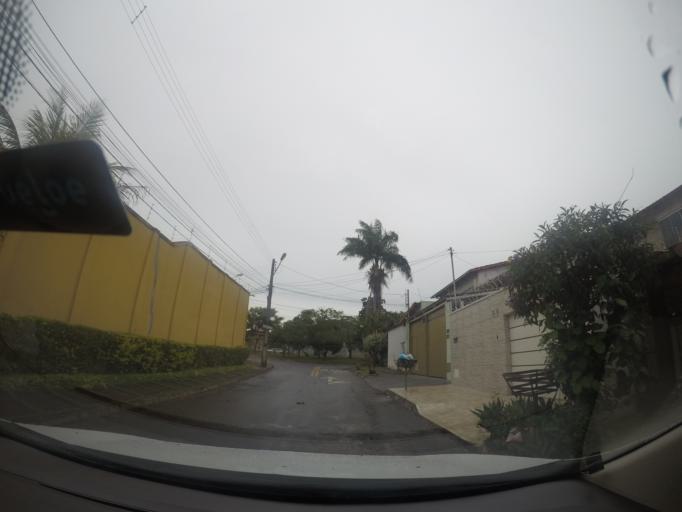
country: BR
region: Goias
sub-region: Goiania
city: Goiania
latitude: -16.6382
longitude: -49.2315
